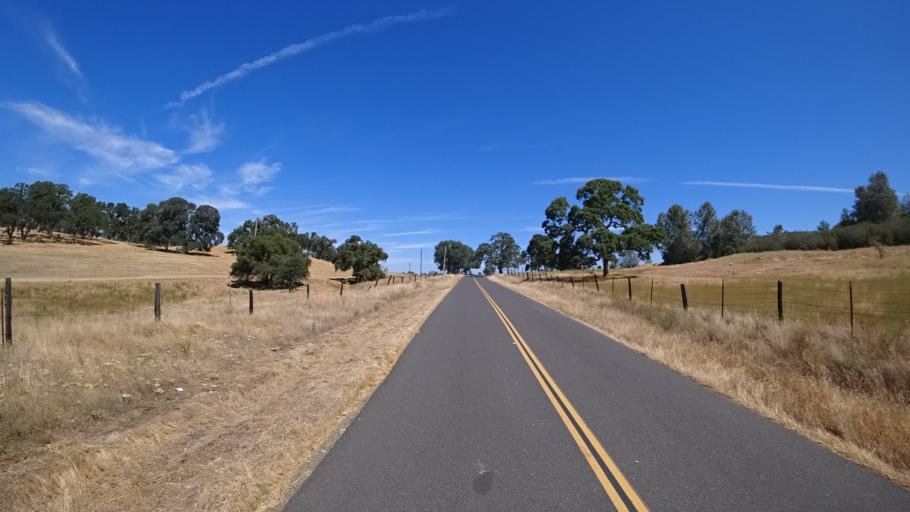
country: US
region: California
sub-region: Calaveras County
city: Angels Camp
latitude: 38.0915
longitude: -120.5567
